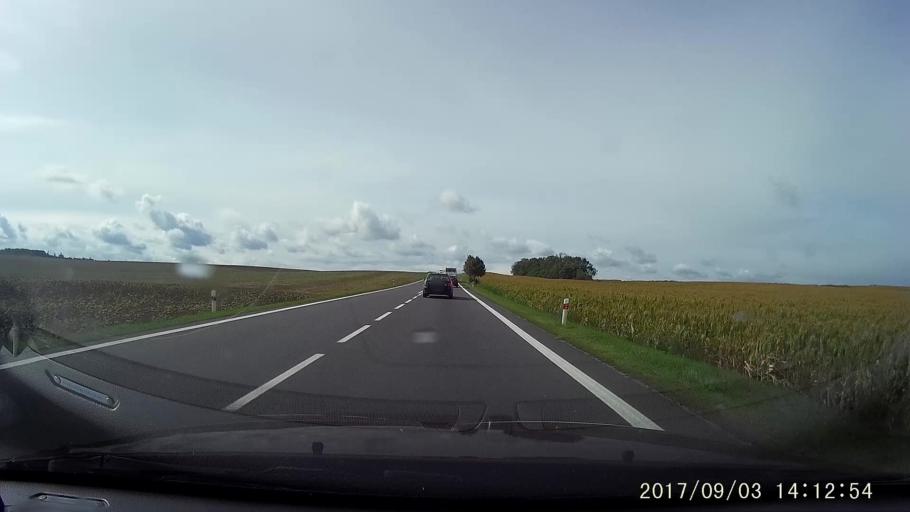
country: CZ
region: South Moravian
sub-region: Okres Znojmo
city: Znojmo
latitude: 48.8740
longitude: 16.0224
